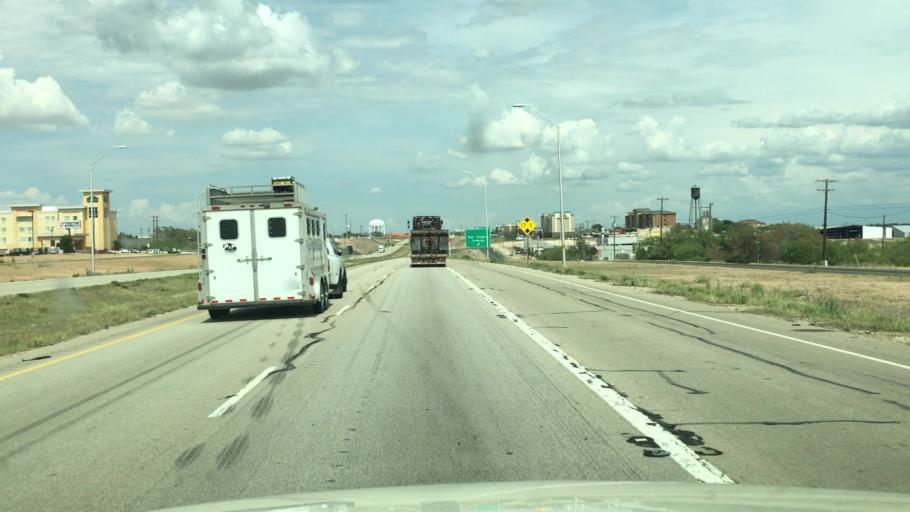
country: US
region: Texas
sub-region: Howard County
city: Big Spring
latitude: 32.2616
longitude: -101.4992
